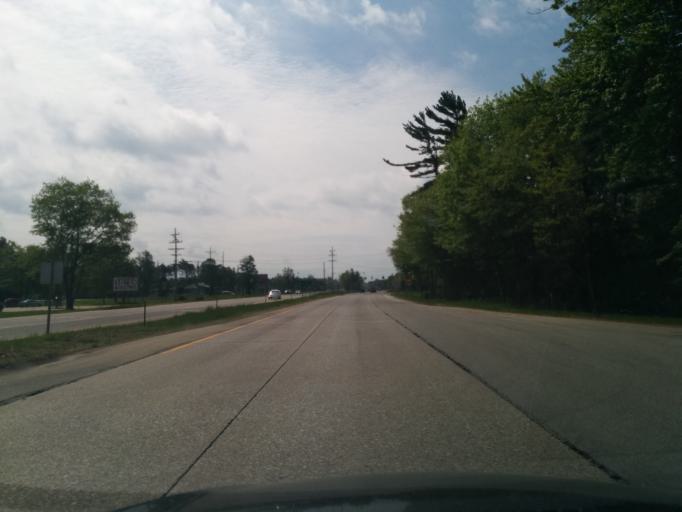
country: US
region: Michigan
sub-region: Ottawa County
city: Grand Haven
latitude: 43.0102
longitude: -86.2065
